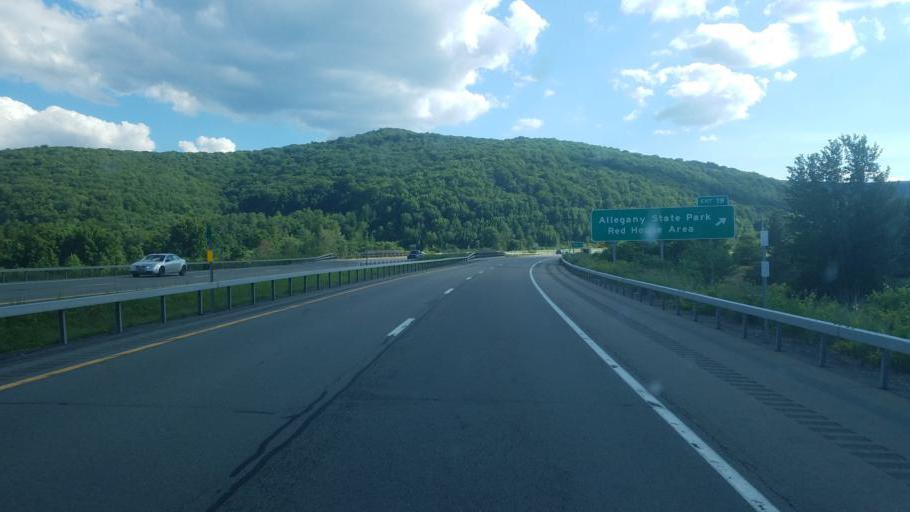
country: US
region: New York
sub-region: Cattaraugus County
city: Salamanca
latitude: 42.1111
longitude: -78.7782
